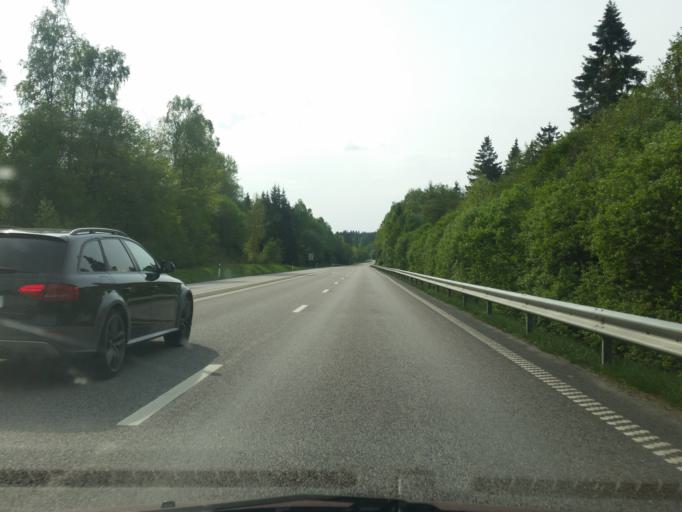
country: SE
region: Vaestra Goetaland
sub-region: Ulricehamns Kommun
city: Ulricehamn
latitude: 57.8033
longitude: 13.3351
